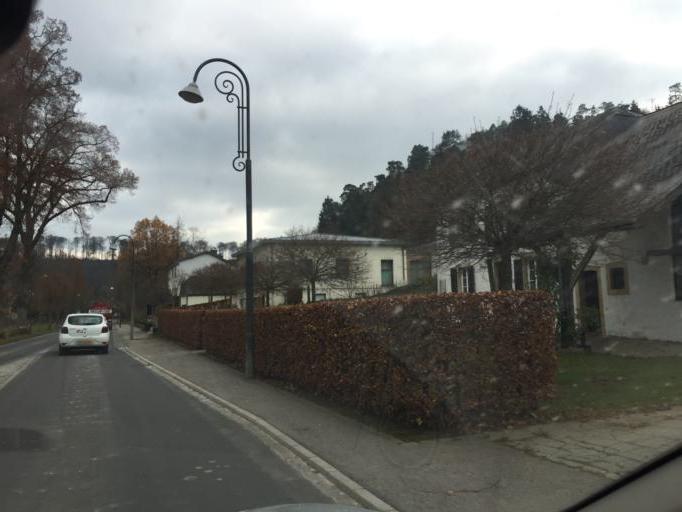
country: LU
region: Diekirch
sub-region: Canton de Redange
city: Saeul
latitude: 49.7307
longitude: 5.9831
